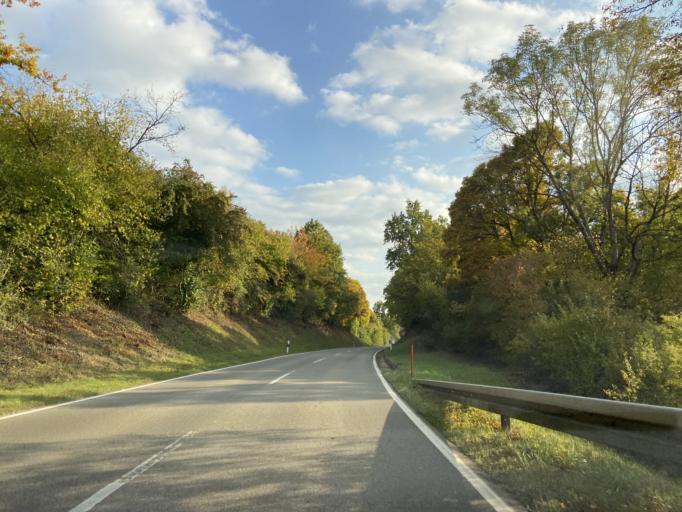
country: DE
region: Baden-Wuerttemberg
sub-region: Tuebingen Region
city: Scheer
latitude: 48.0809
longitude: 9.2933
